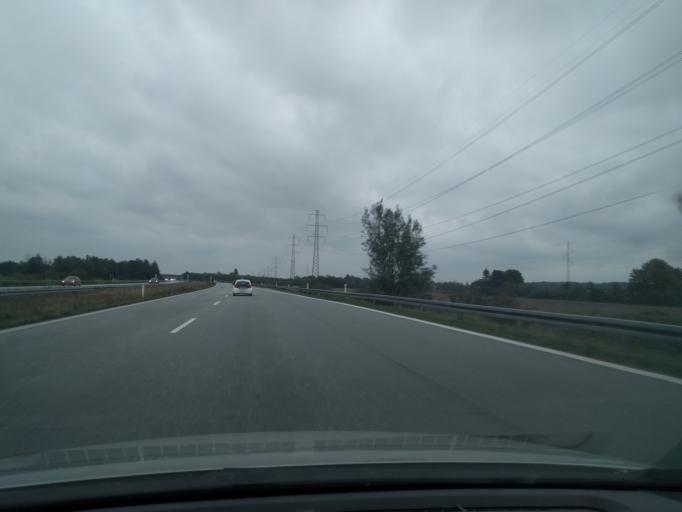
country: DK
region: Zealand
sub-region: Ringsted Kommune
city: Ringsted
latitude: 55.4563
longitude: 11.8606
